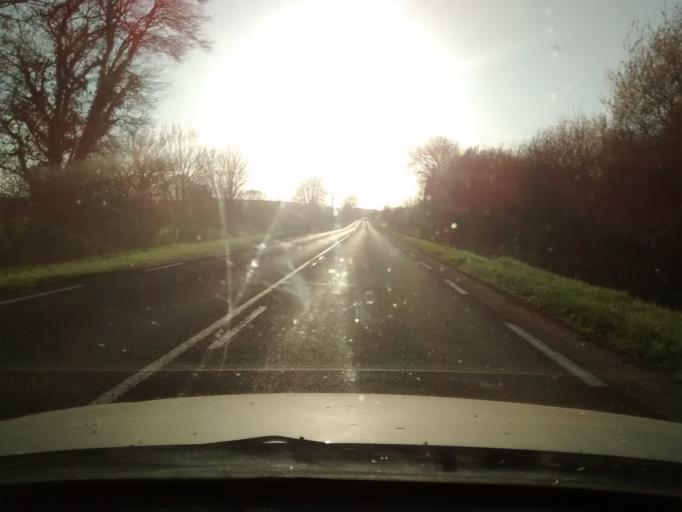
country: FR
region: Pays de la Loire
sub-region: Departement de la Sarthe
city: Coulans-sur-Gee
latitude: 48.0199
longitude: -0.0597
